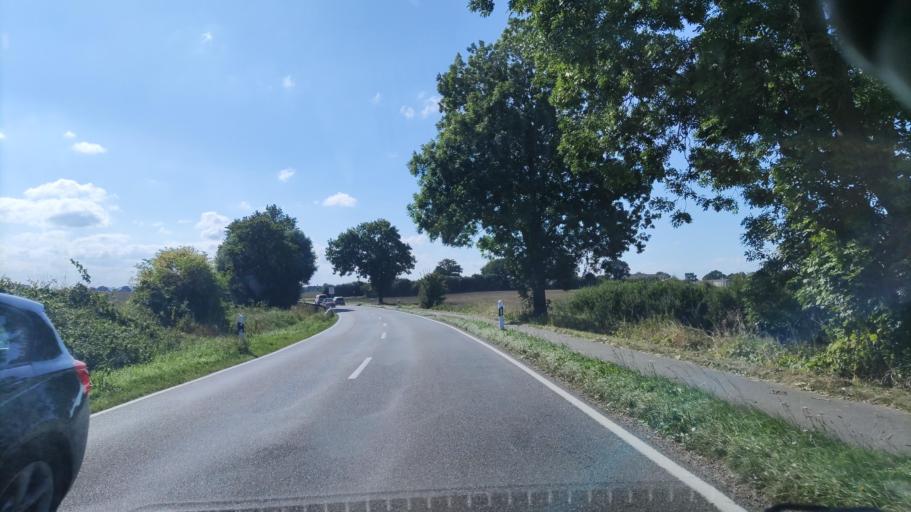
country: DE
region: Schleswig-Holstein
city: Osterby
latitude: 54.4580
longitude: 9.7709
